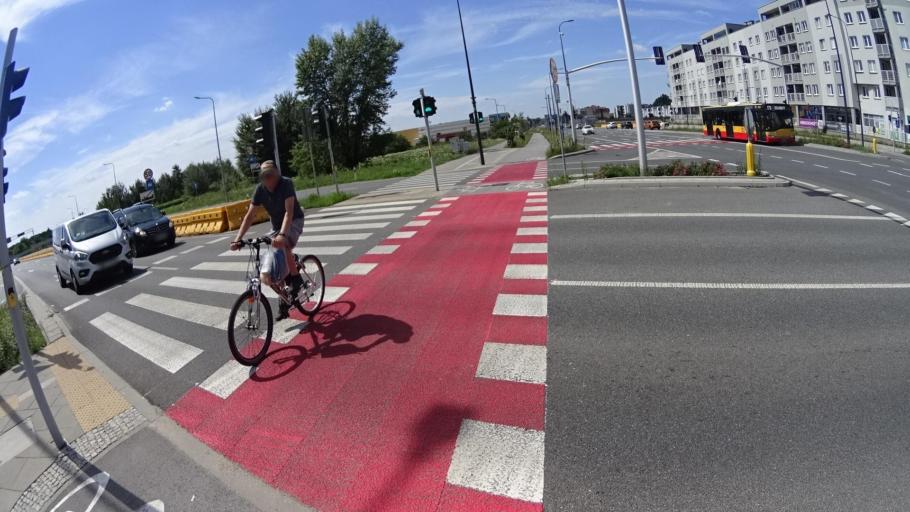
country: PL
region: Masovian Voivodeship
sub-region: Warszawa
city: Ursynow
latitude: 52.1415
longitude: 21.0303
